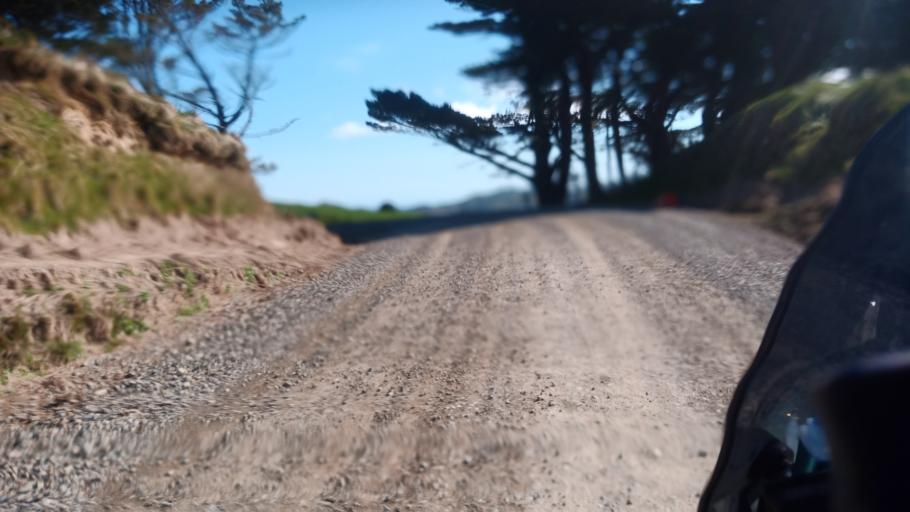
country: NZ
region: Gisborne
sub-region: Gisborne District
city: Gisborne
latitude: -39.1614
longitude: 177.9026
